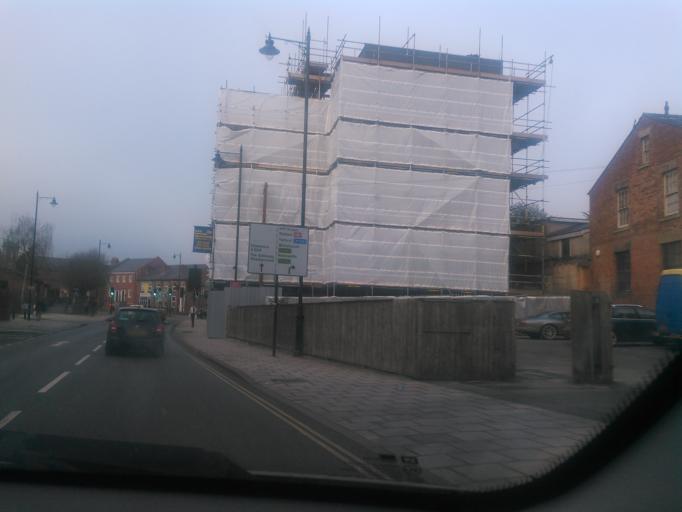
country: GB
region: England
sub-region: Shropshire
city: Shrewsbury
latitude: 52.7120
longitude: -2.7508
